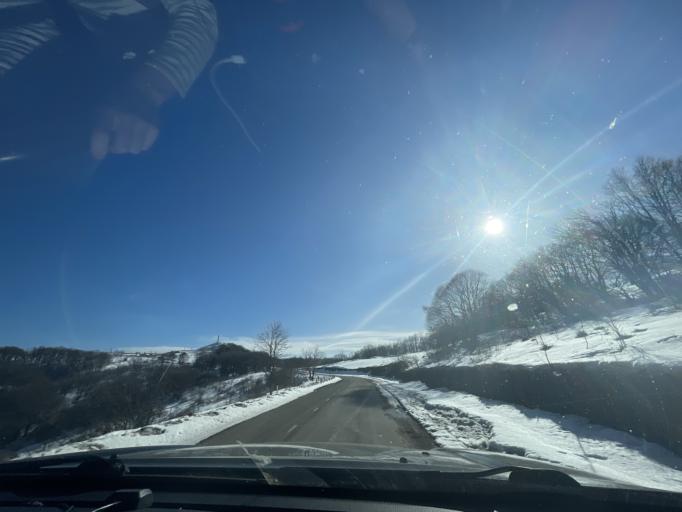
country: GE
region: Kvemo Kartli
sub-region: Tetri Tsqaro
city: Manglisi
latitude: 41.7663
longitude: 44.5066
